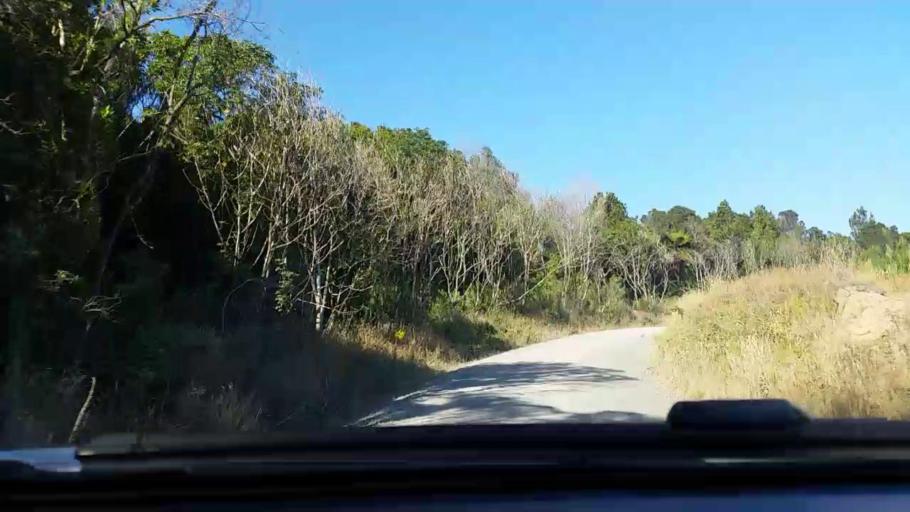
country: NZ
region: Bay of Plenty
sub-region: Kawerau District
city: Kawerau
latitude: -37.9917
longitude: 176.5285
